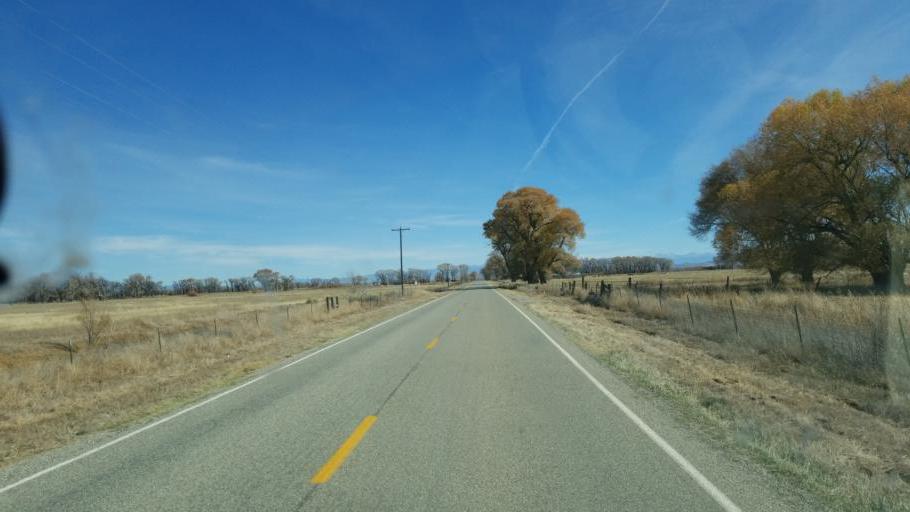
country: US
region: Colorado
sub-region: Conejos County
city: Conejos
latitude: 37.2834
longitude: -106.0527
